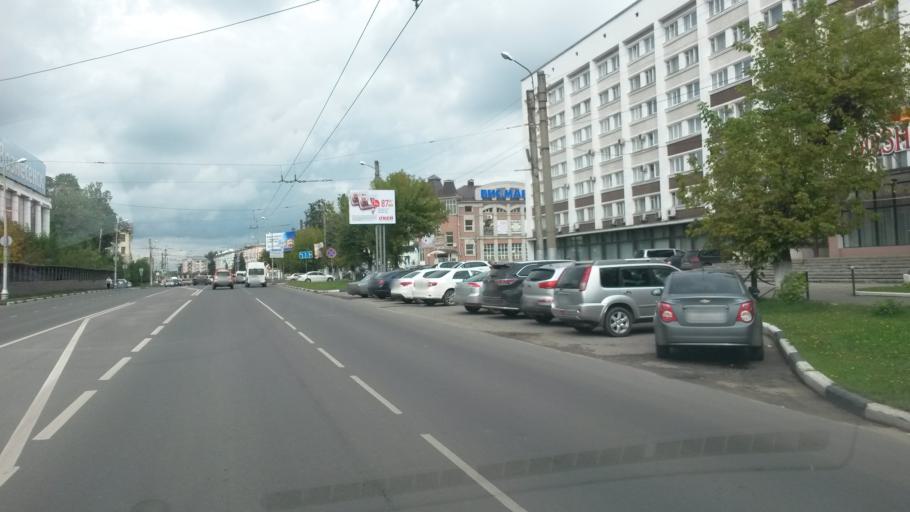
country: RU
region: Ivanovo
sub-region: Gorod Ivanovo
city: Ivanovo
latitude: 57.0085
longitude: 40.9726
